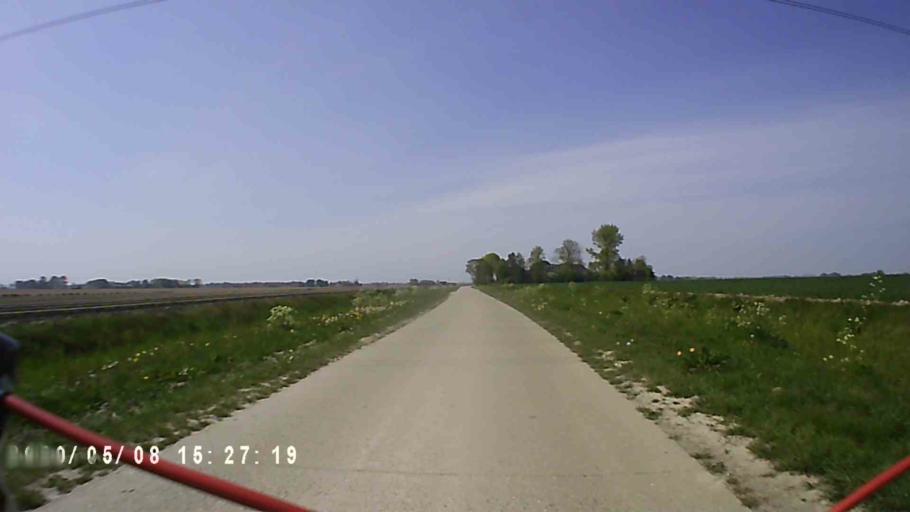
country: NL
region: Groningen
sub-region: Gemeente Appingedam
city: Appingedam
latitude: 53.3606
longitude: 6.7483
